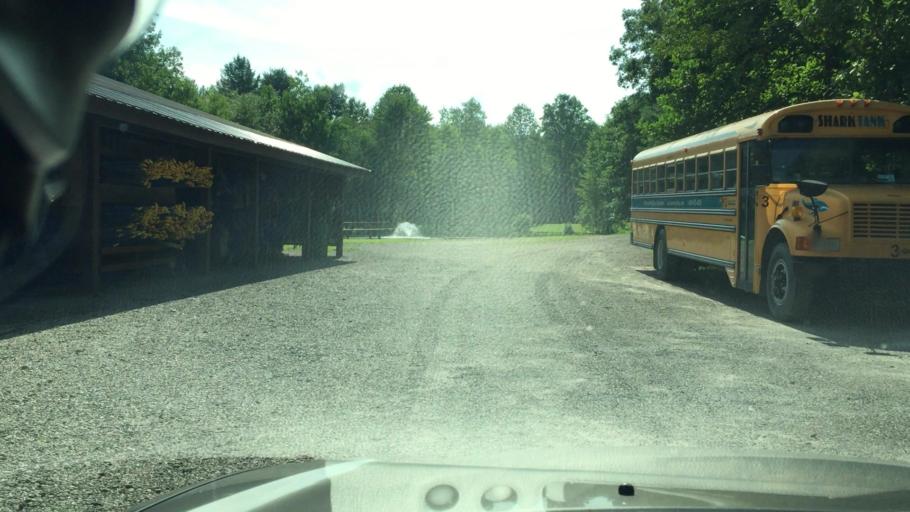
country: US
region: Pennsylvania
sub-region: Carbon County
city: Nesquehoning
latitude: 40.8698
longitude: -75.7967
